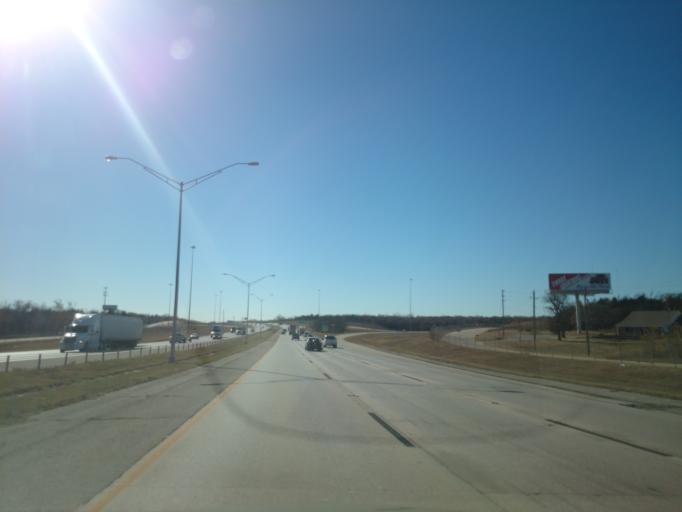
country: US
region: Oklahoma
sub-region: Oklahoma County
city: Spencer
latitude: 35.5686
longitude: -97.4496
